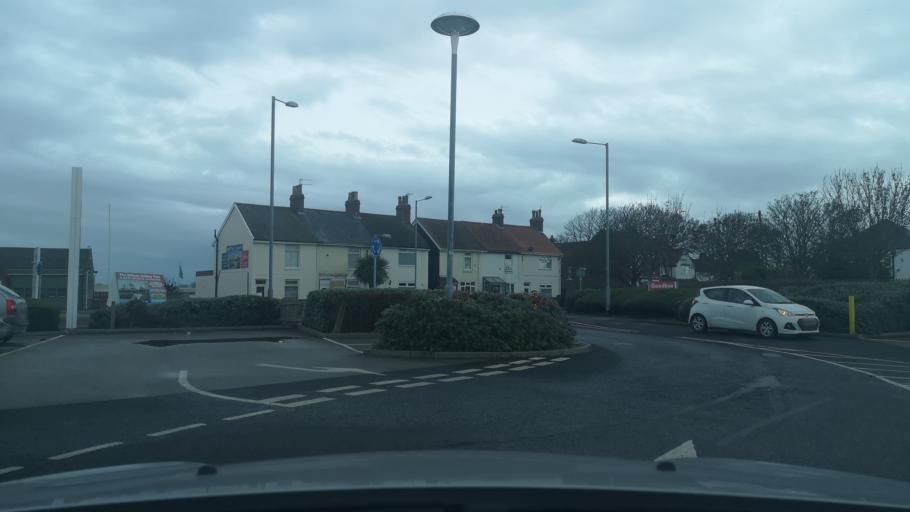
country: GB
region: England
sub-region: East Riding of Yorkshire
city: Withernsea
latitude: 53.7237
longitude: 0.0365
